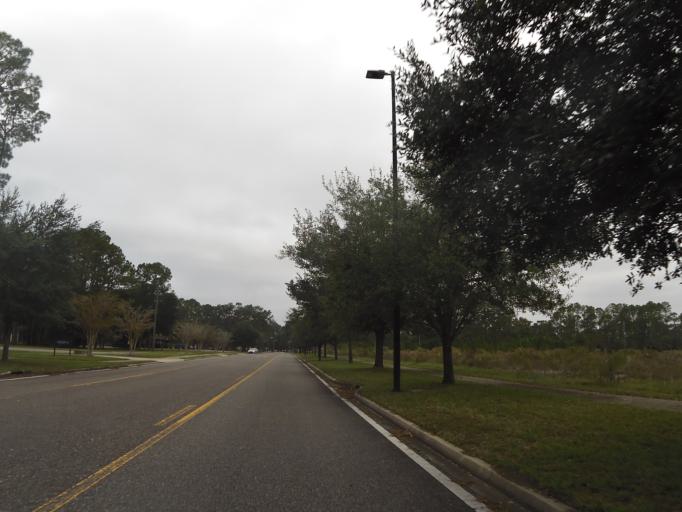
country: US
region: Florida
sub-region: Duval County
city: Baldwin
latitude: 30.2337
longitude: -81.8873
